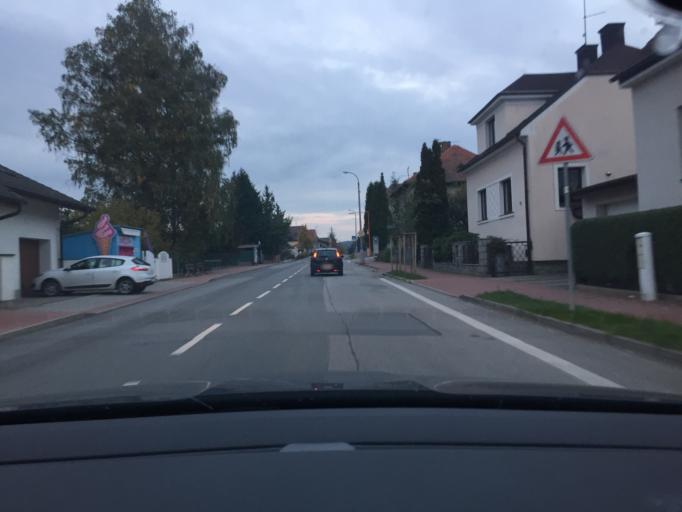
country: CZ
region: Jihocesky
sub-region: Okres Ceske Budejovice
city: Hluboka nad Vltavou
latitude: 49.0548
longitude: 14.4514
